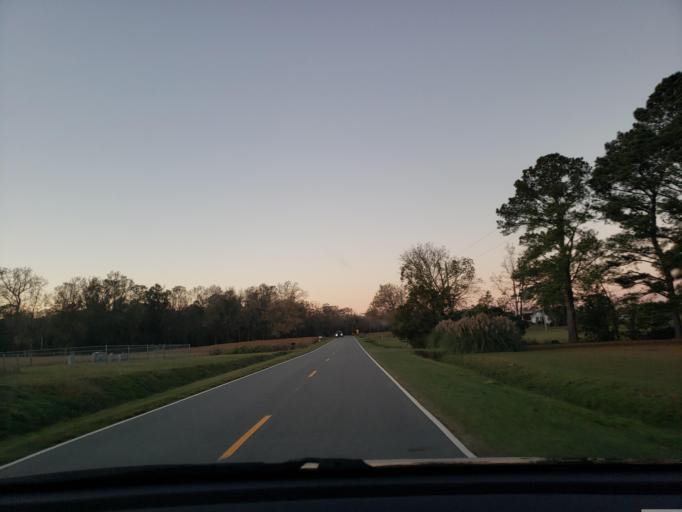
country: US
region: North Carolina
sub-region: Duplin County
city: Beulaville
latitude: 34.7545
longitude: -77.7064
